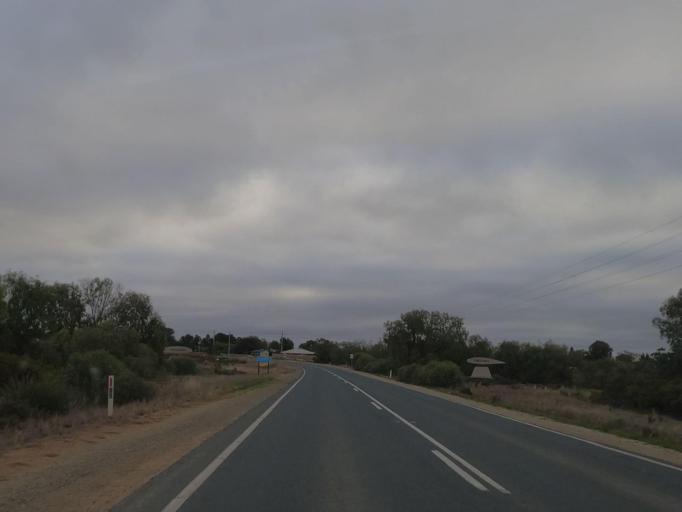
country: AU
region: Victoria
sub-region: Swan Hill
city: Swan Hill
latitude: -35.4676
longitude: 143.6580
